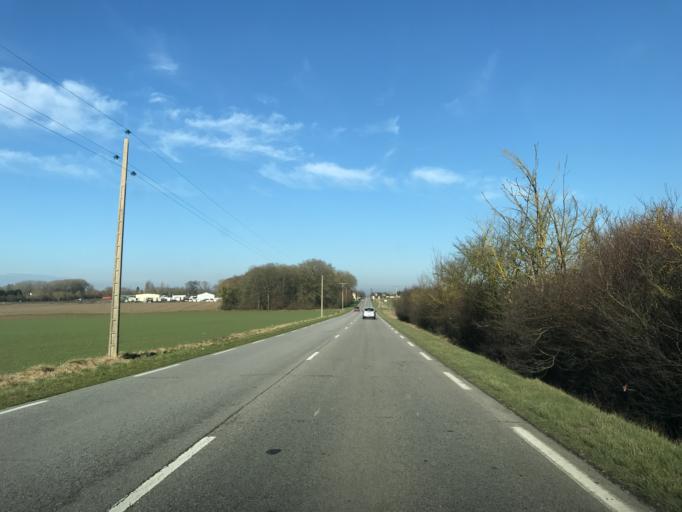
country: FR
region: Haute-Normandie
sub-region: Departement de l'Eure
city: Ande
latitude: 49.2013
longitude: 1.2311
